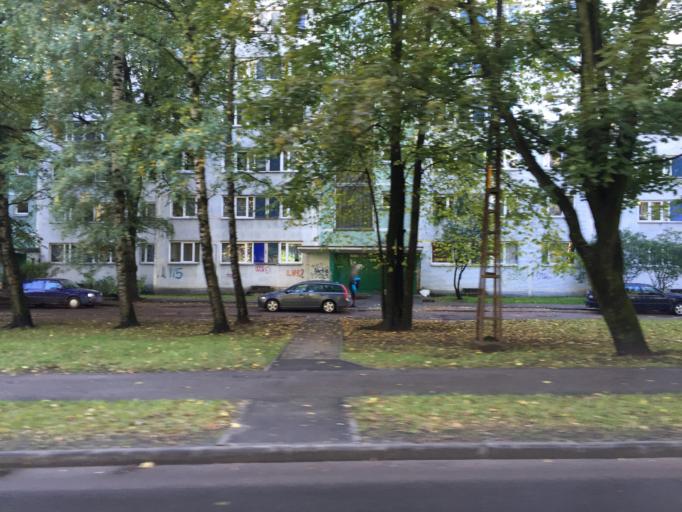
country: LV
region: Marupe
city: Marupe
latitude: 56.9481
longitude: 24.0586
